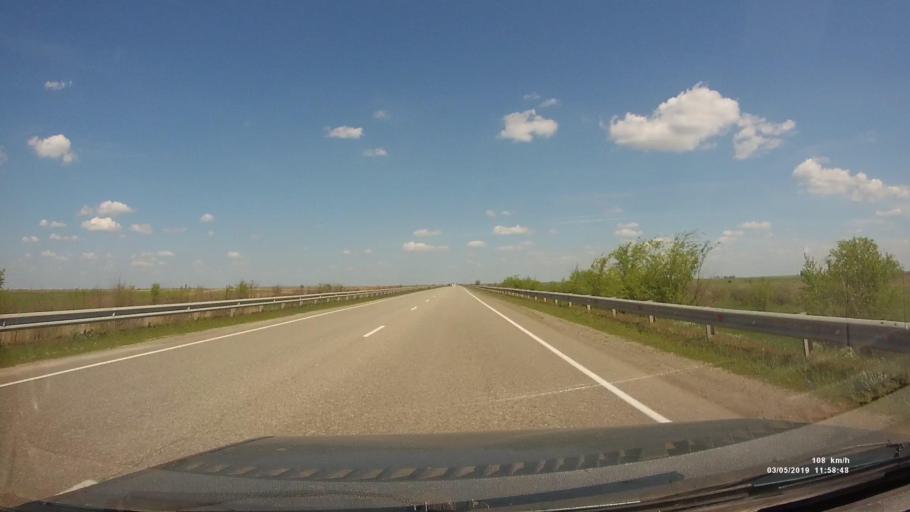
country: RU
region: Rostov
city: Bagayevskaya
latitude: 47.2258
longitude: 40.3237
